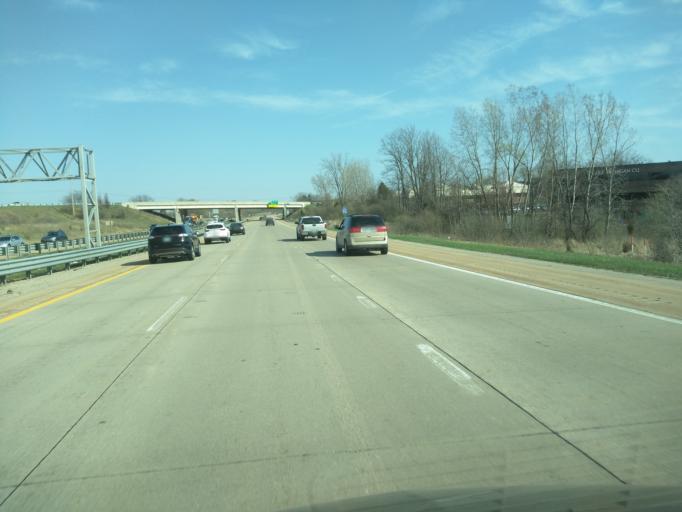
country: US
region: Michigan
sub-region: Kent County
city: Forest Hills
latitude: 42.9098
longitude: -85.5320
